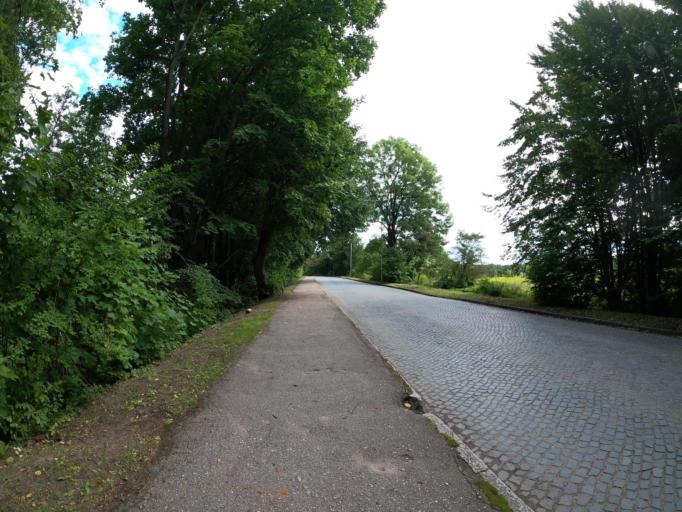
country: RU
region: Kaliningrad
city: Zheleznodorozhnyy
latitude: 54.3540
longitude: 21.3132
